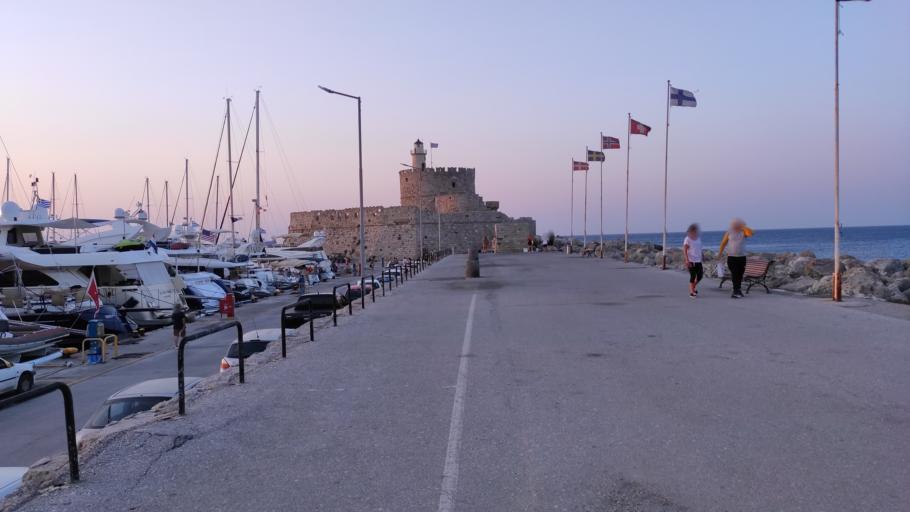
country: GR
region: South Aegean
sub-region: Nomos Dodekanisou
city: Rodos
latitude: 36.4498
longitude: 28.2279
